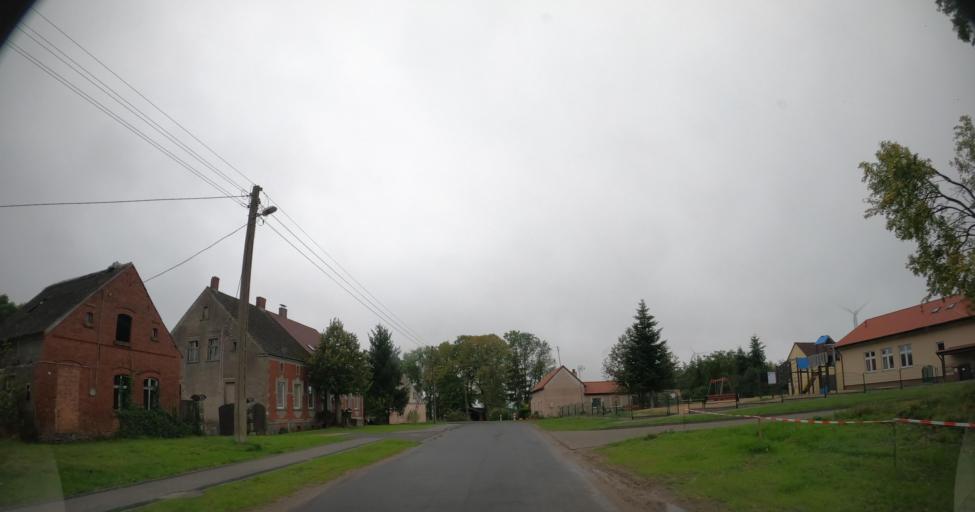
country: PL
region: West Pomeranian Voivodeship
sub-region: Powiat pyrzycki
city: Kozielice
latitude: 53.0722
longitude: 14.7869
